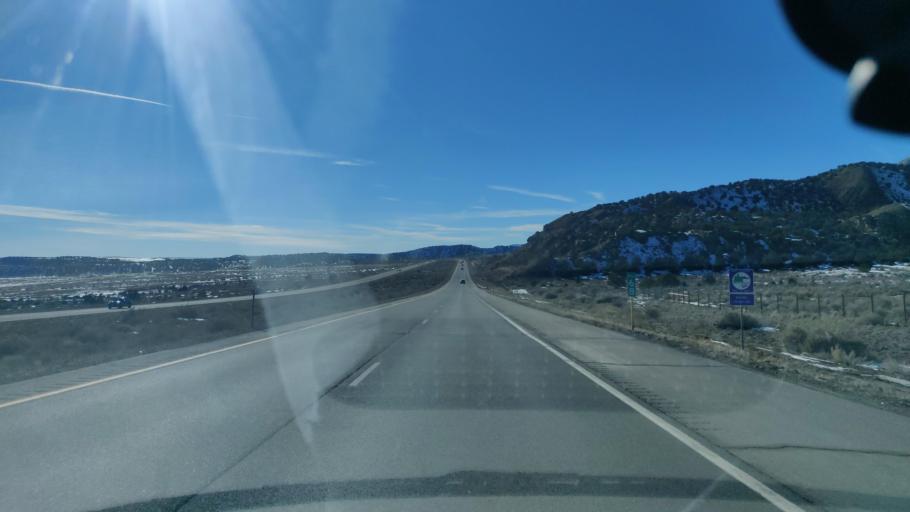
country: US
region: Colorado
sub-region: Garfield County
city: Parachute
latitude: 39.3906
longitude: -108.1341
